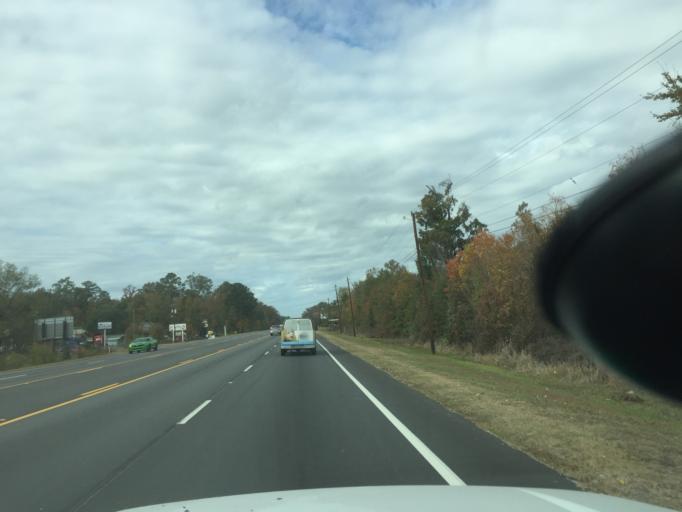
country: US
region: Georgia
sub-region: Chatham County
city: Garden City
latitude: 32.0904
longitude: -81.1863
